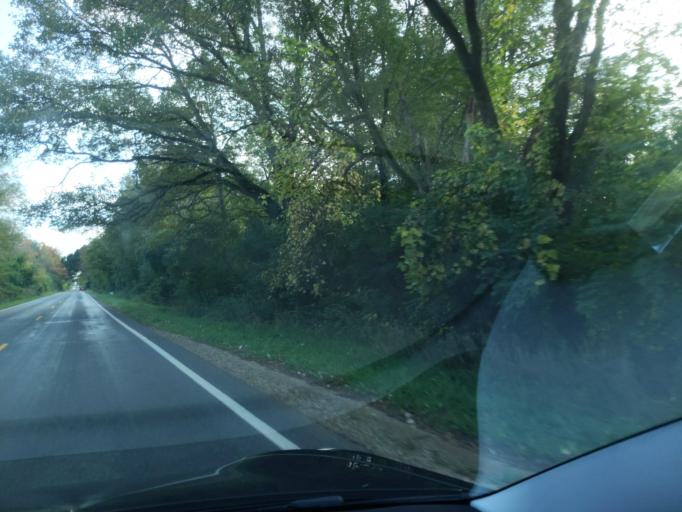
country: US
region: Michigan
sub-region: Jackson County
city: Jackson
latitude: 42.3199
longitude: -84.4628
